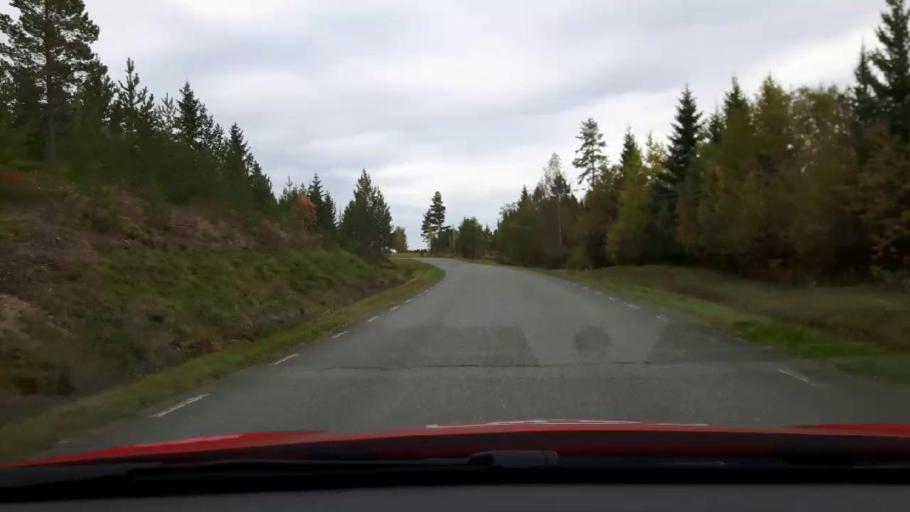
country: SE
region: Jaemtland
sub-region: Krokoms Kommun
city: Krokom
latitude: 63.2376
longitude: 14.1149
